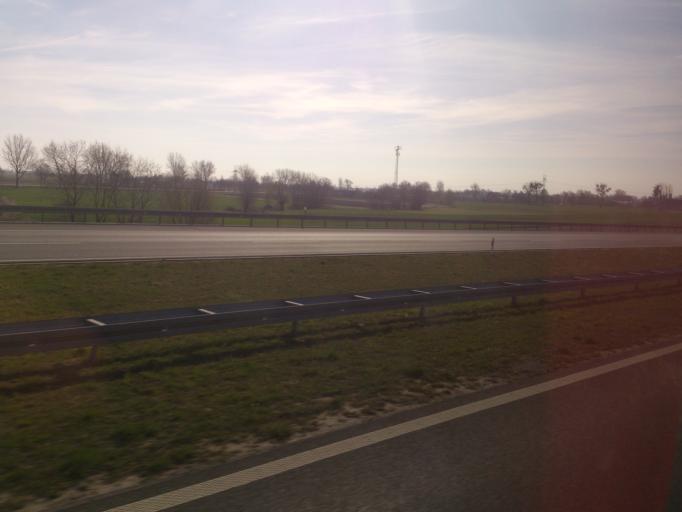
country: PL
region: Kujawsko-Pomorskie
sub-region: Powiat aleksandrowski
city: Waganiec
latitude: 52.7901
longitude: 18.8406
